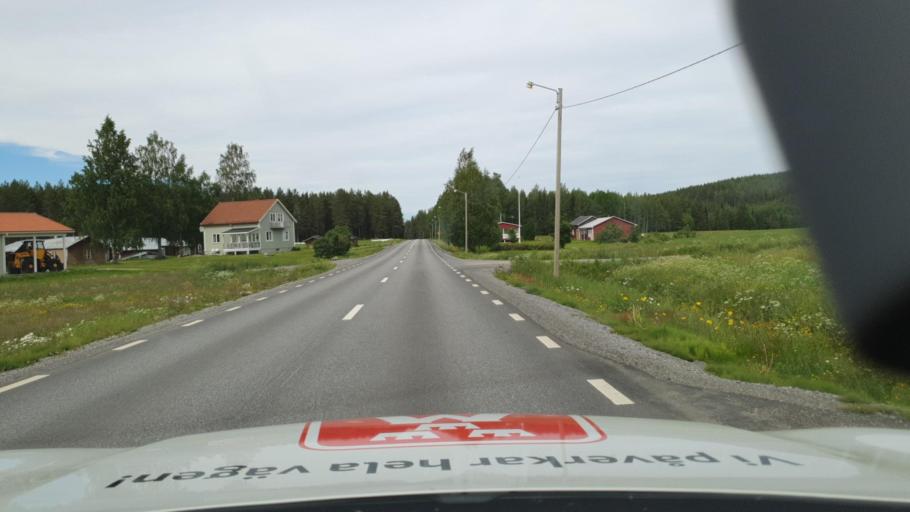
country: SE
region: Vaesterbotten
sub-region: Skelleftea Kommun
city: Burtraesk
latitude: 64.4932
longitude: 20.6263
